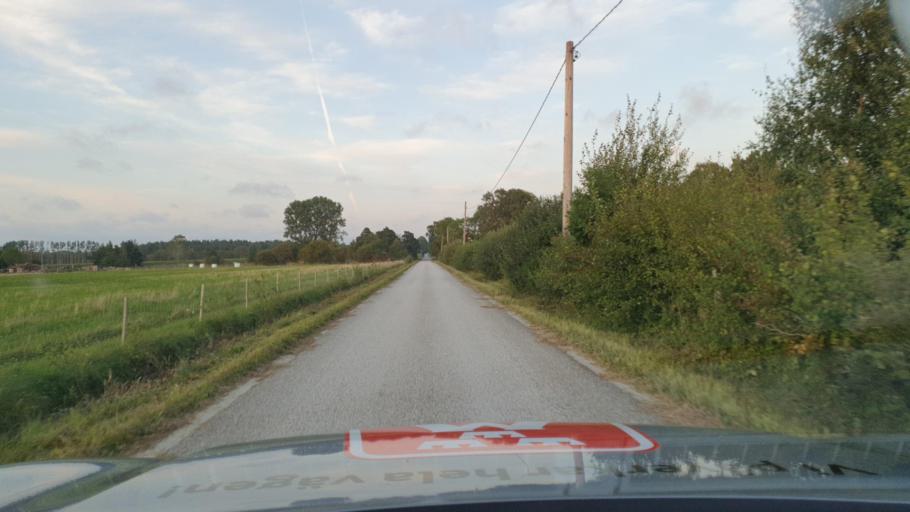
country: SE
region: Gotland
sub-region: Gotland
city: Klintehamn
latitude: 57.2770
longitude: 18.1408
